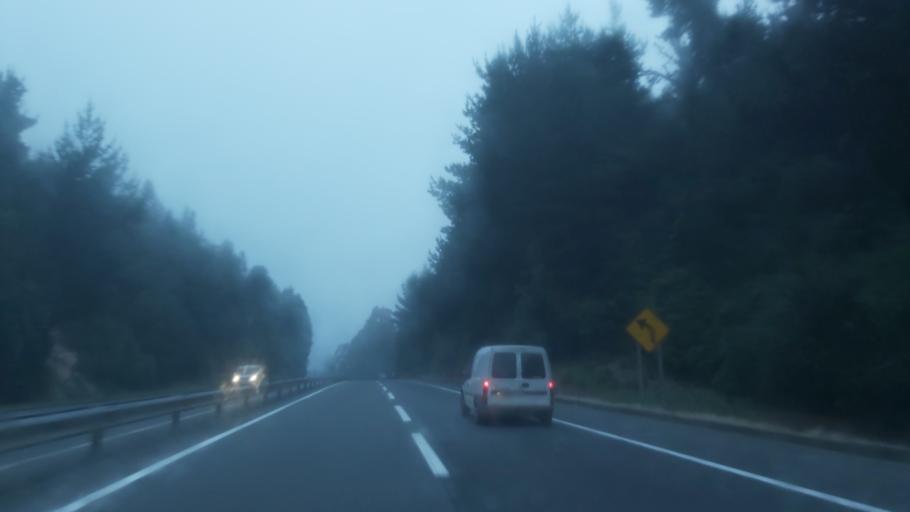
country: CL
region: Biobio
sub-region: Provincia de Concepcion
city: Penco
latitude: -36.7420
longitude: -72.9067
